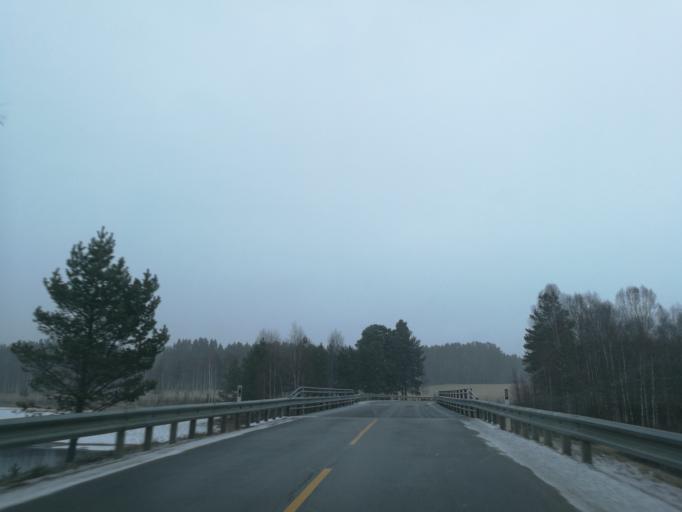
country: NO
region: Hedmark
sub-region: Asnes
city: Flisa
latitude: 60.7057
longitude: 12.3588
